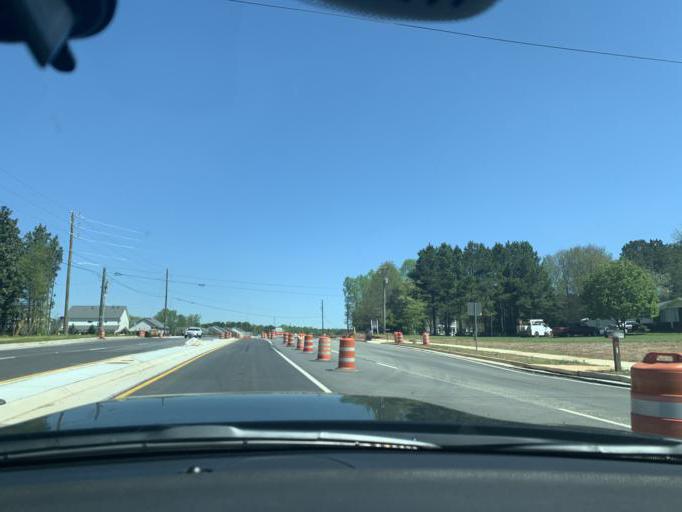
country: US
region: Georgia
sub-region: Forsyth County
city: Cumming
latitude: 34.2179
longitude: -84.1983
